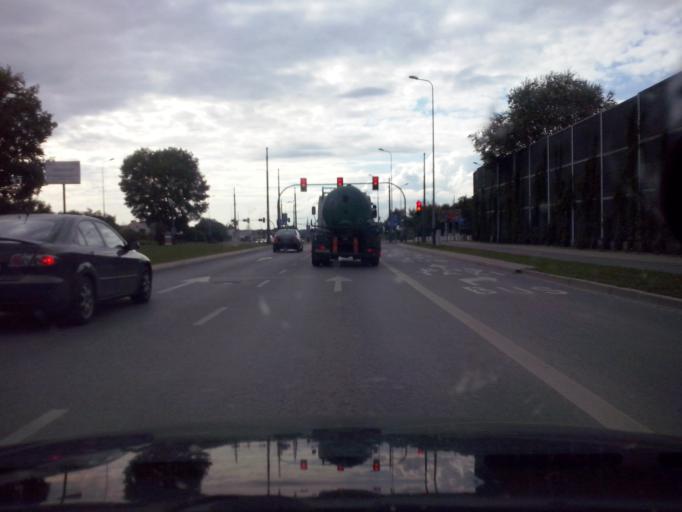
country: PL
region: Lesser Poland Voivodeship
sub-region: Krakow
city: Krakow
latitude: 50.0396
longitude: 20.0025
